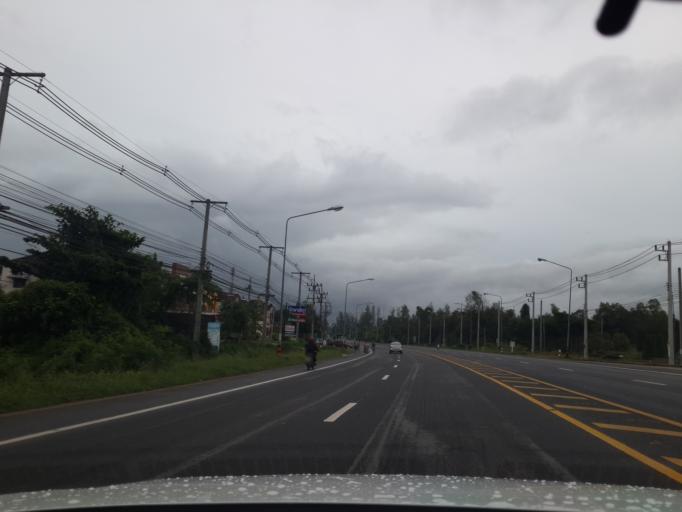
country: TH
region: Songkhla
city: Khlong Hoi Khong
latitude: 6.9520
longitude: 100.4181
